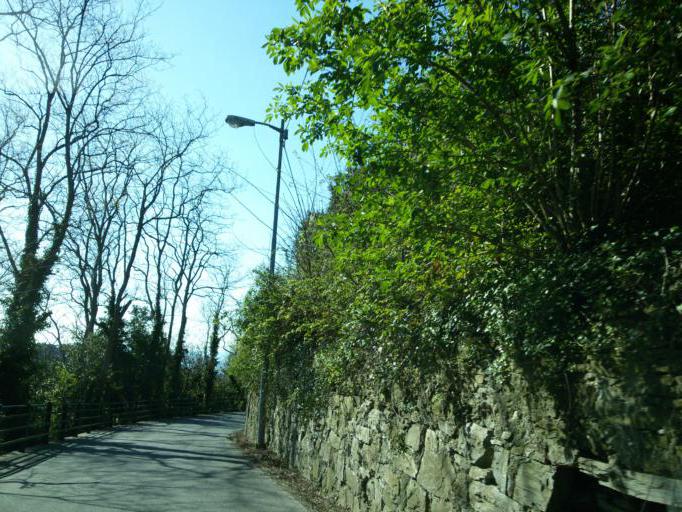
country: IT
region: Liguria
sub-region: Provincia di Genova
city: Genoa
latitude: 44.4264
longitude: 8.9032
